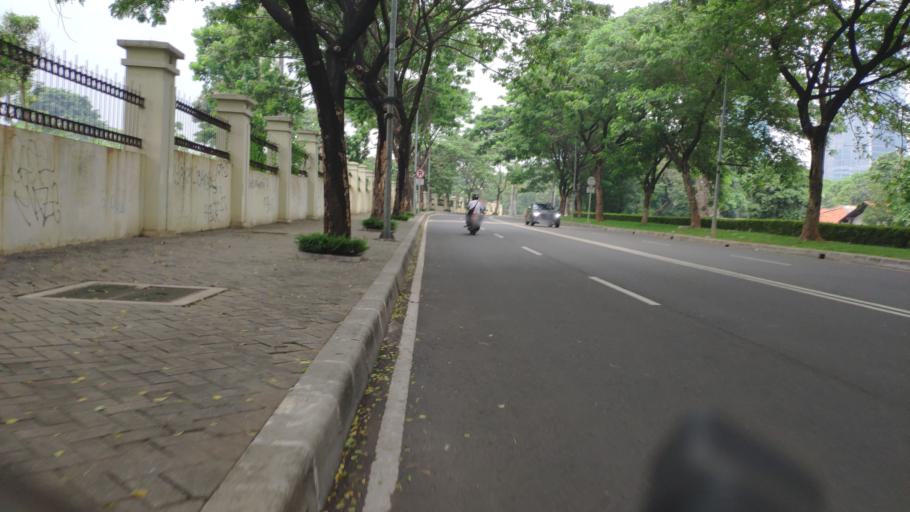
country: ID
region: Jakarta Raya
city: Jakarta
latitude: -6.2229
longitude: 106.8359
